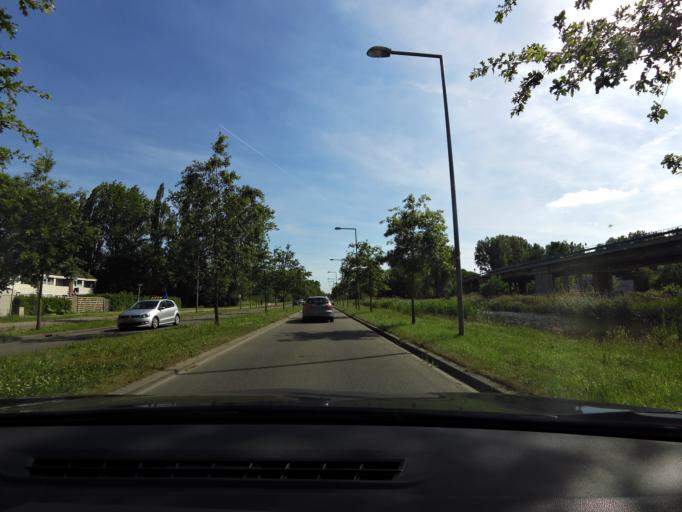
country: NL
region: South Holland
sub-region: Gemeente Rotterdam
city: Delfshaven
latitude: 51.8703
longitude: 4.4771
